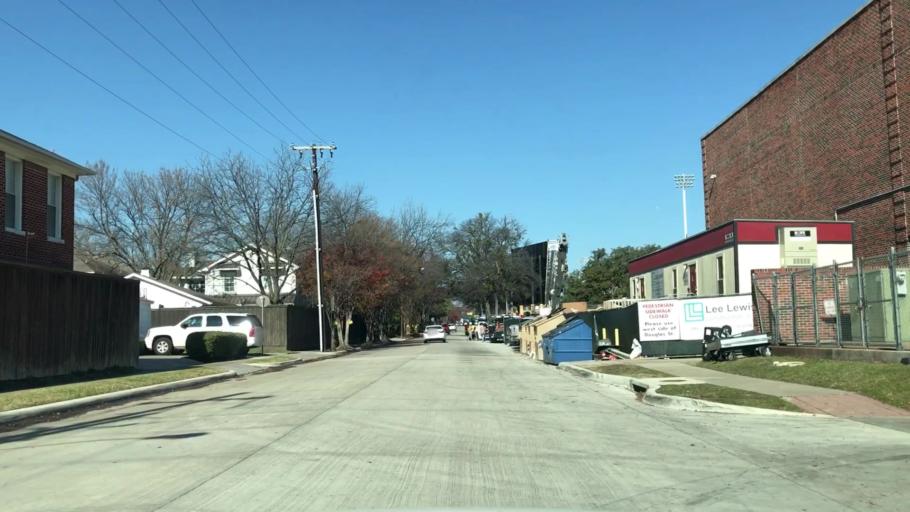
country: US
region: Texas
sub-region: Dallas County
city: University Park
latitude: 32.8474
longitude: -96.8085
